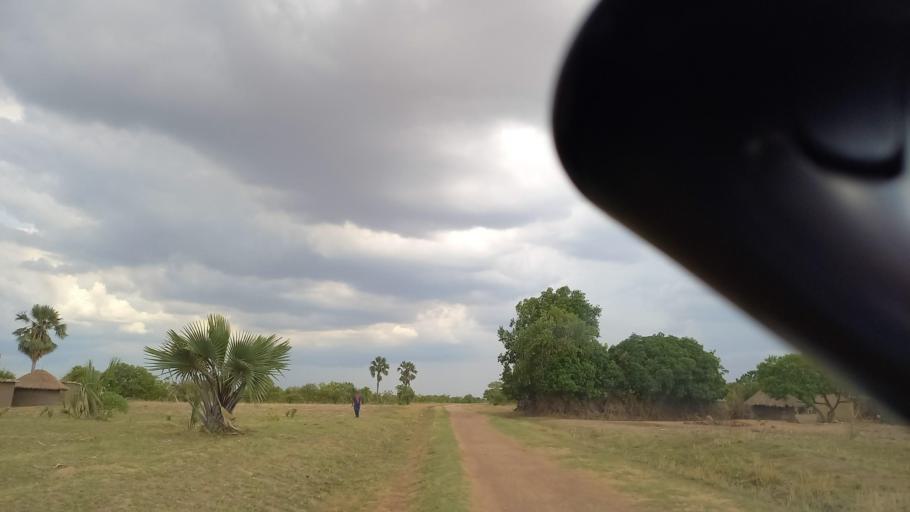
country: ZM
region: Lusaka
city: Kafue
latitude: -15.8376
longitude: 28.0844
